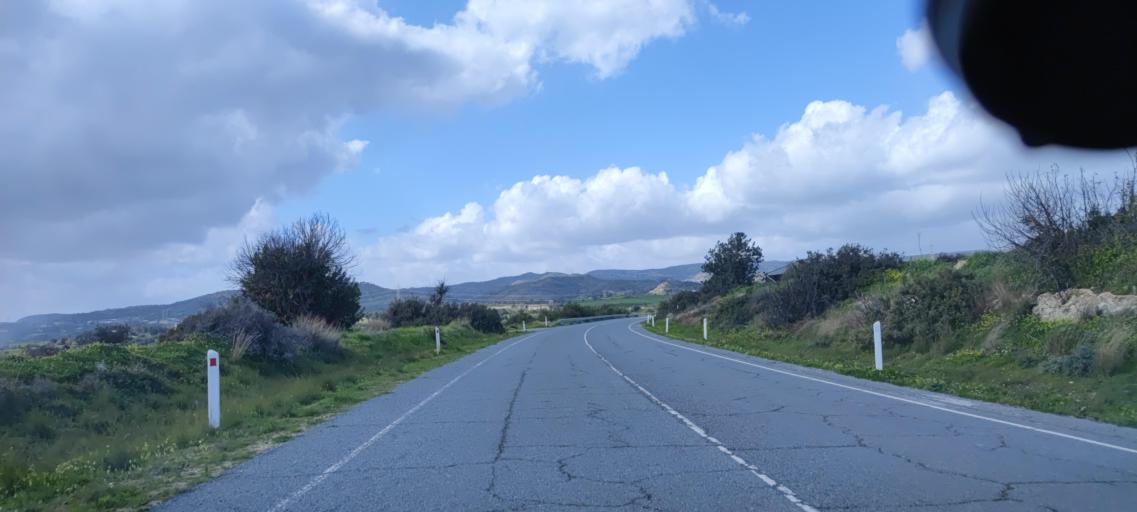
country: CY
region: Limassol
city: Pissouri
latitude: 34.6801
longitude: 32.7508
